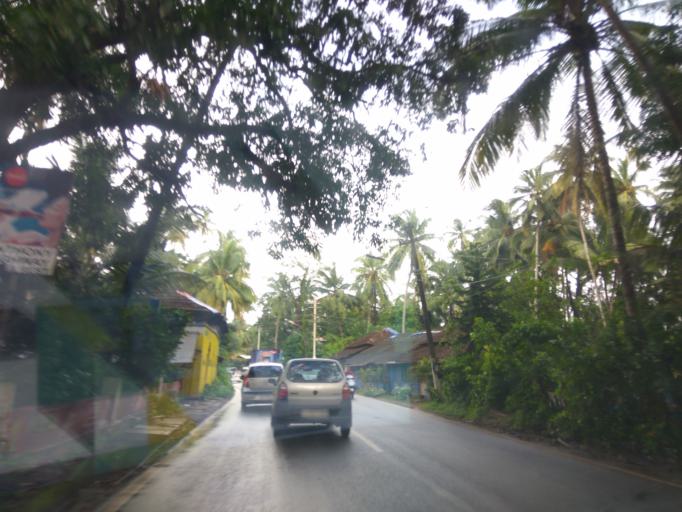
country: IN
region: Goa
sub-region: North Goa
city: Goa Velha
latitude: 15.4406
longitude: 73.8696
